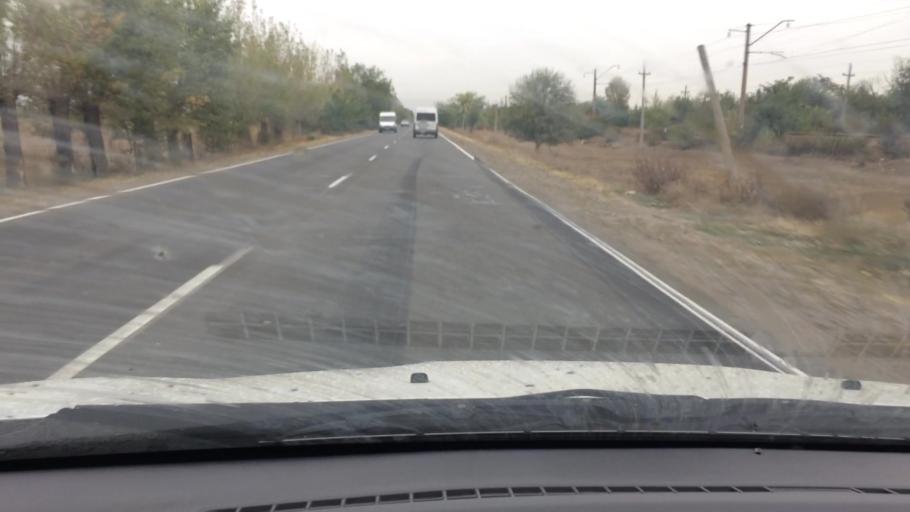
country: GE
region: Kvemo Kartli
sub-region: Marneuli
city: Marneuli
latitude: 41.4433
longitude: 44.8165
